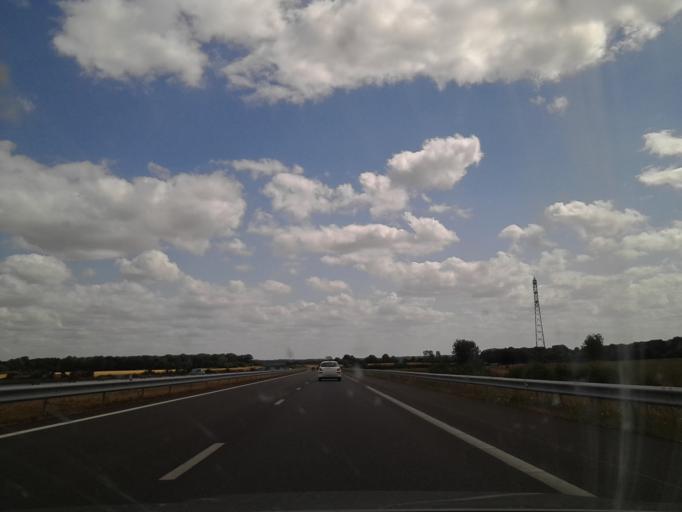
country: FR
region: Centre
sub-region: Departement du Cher
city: Orval
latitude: 46.8131
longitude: 2.4125
